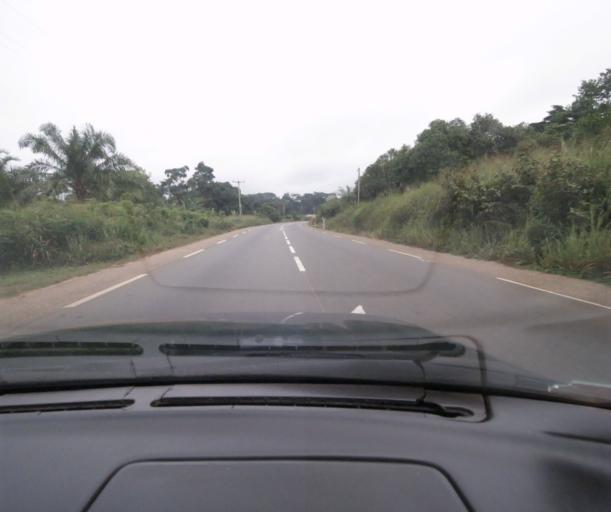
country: CM
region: Centre
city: Obala
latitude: 4.2114
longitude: 11.4422
